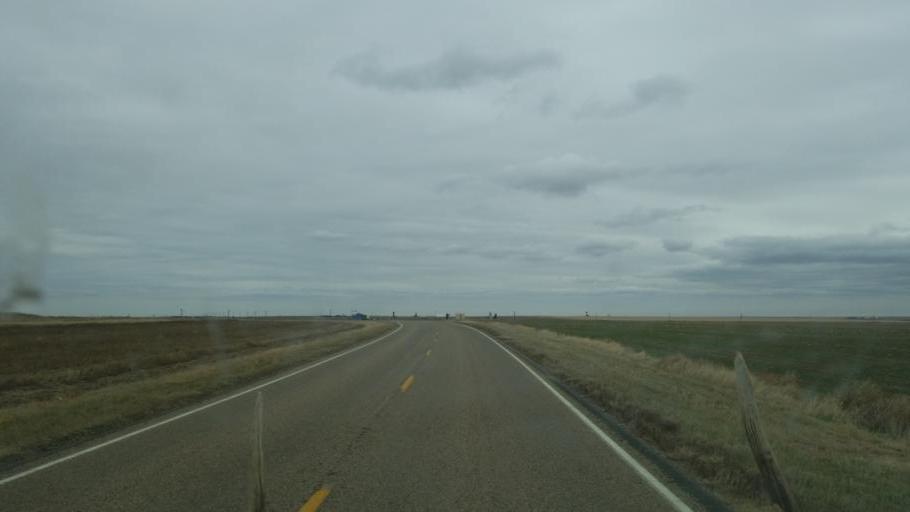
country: US
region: Colorado
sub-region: Cheyenne County
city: Cheyenne Wells
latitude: 38.8452
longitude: -102.1359
